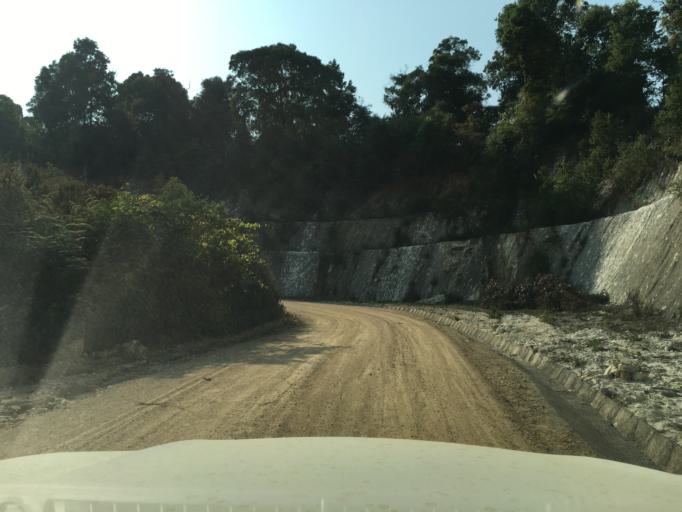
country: LA
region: Houaphan
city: Huameung
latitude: 20.1806
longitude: 103.8329
